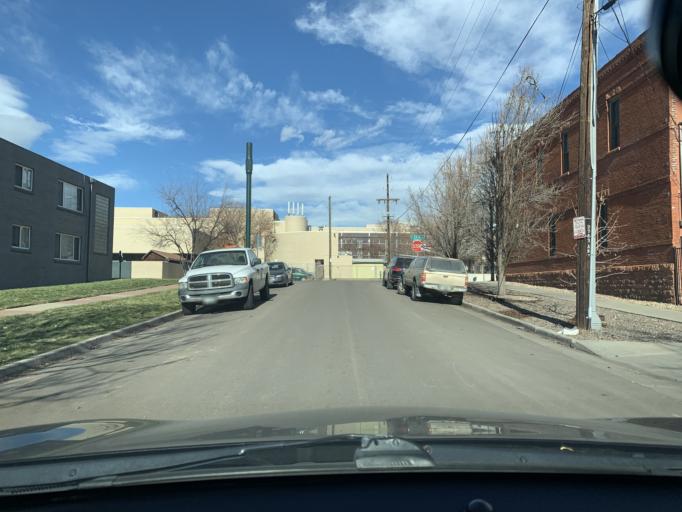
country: US
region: Colorado
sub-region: Denver County
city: Denver
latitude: 39.7544
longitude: -105.0221
